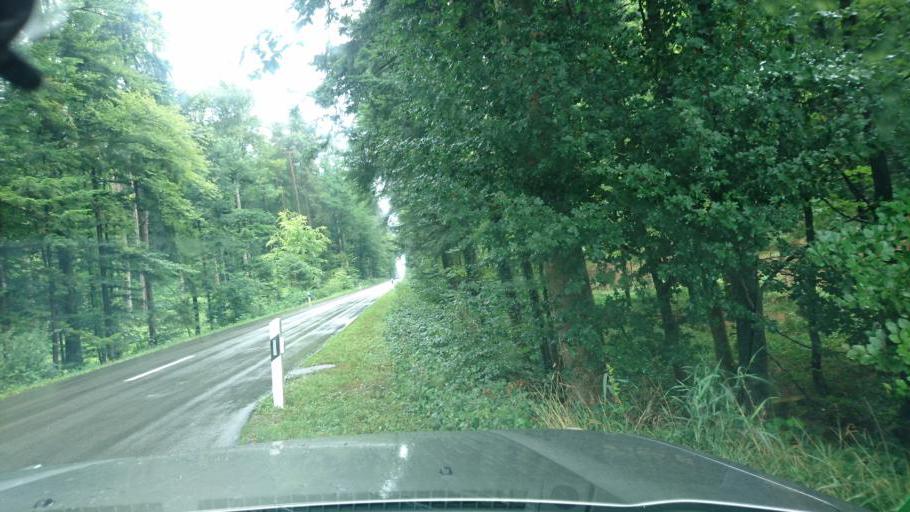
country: CH
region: Zurich
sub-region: Bezirk Andelfingen
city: Henggart
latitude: 47.5650
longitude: 8.7009
